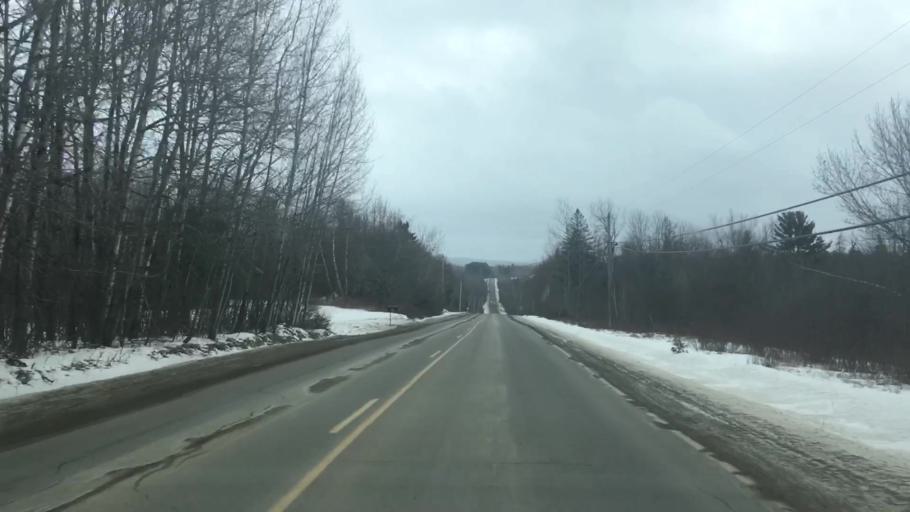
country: US
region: Maine
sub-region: Washington County
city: East Machias
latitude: 44.9724
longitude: -67.4489
